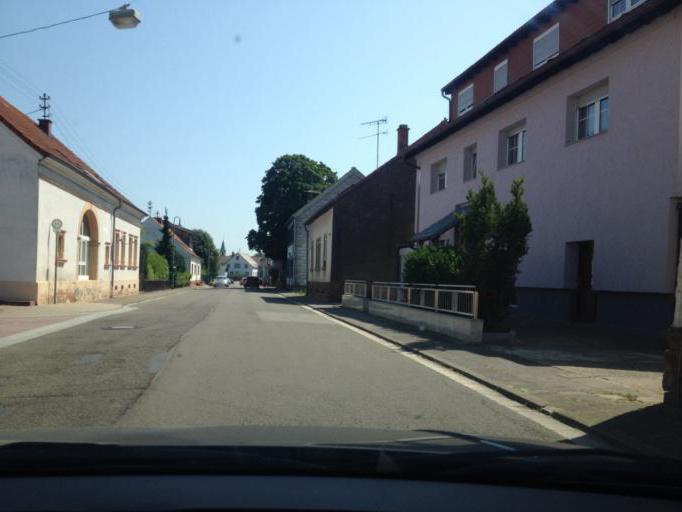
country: DE
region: Rheinland-Pfalz
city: Hutschenhausen
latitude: 49.4182
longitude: 7.4694
